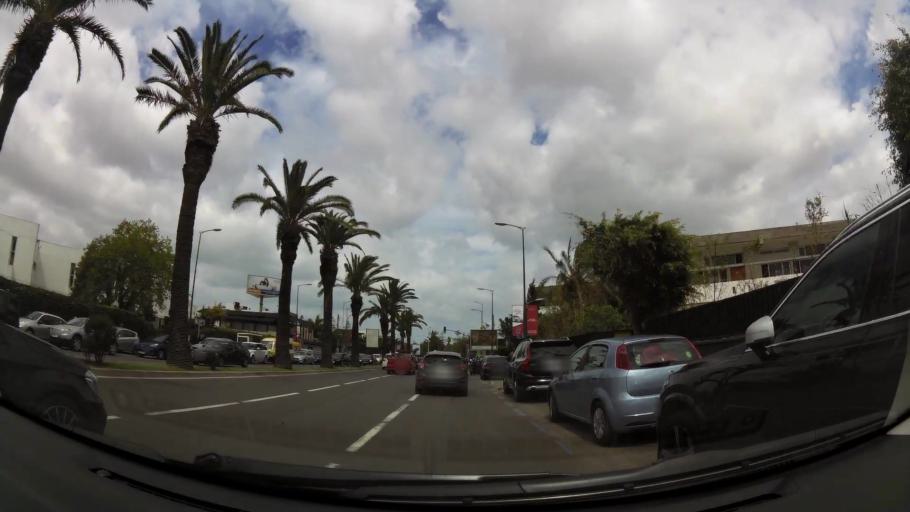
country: MA
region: Grand Casablanca
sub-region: Casablanca
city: Casablanca
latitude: 33.5782
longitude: -7.6545
